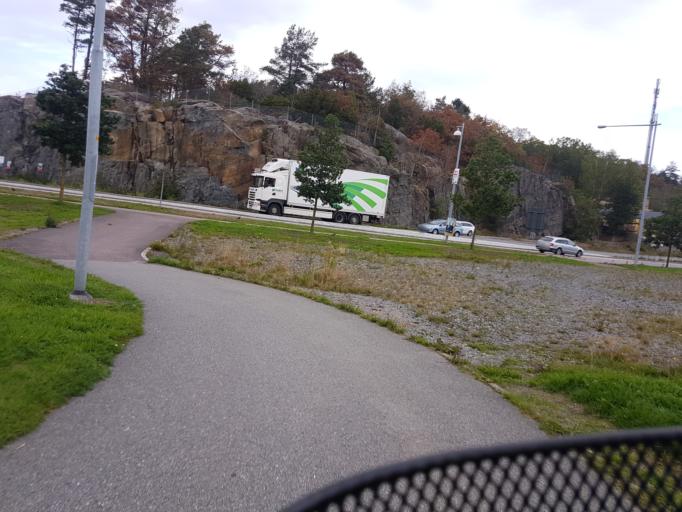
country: SE
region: Vaestra Goetaland
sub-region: Ale Kommun
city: Nodinge-Nol
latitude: 57.8962
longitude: 12.0478
